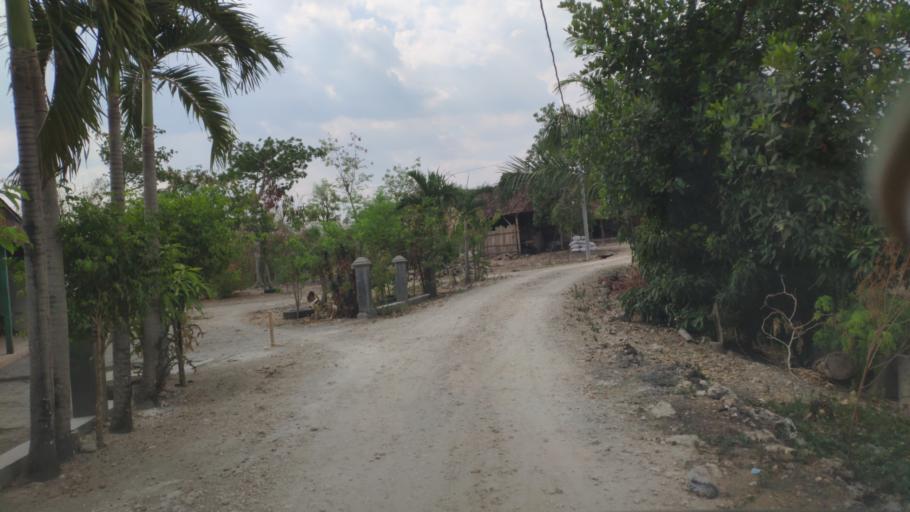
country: ID
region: Central Java
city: Randublatung
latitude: -7.3024
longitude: 111.3382
